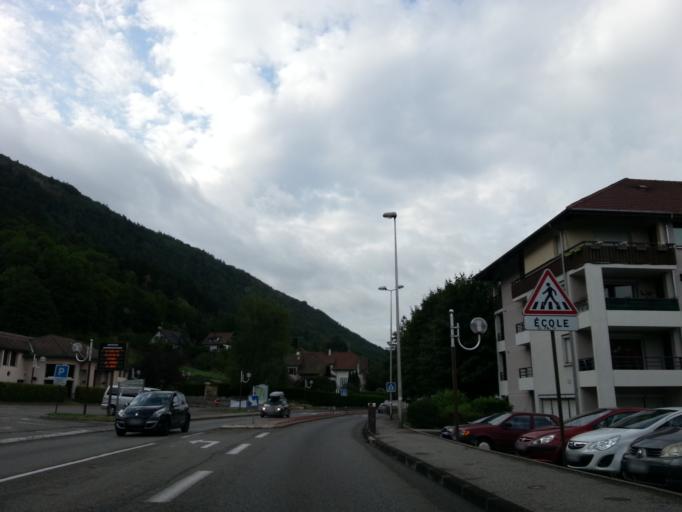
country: FR
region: Rhone-Alpes
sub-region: Departement de la Haute-Savoie
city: Sevrier
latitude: 45.8649
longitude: 6.1400
